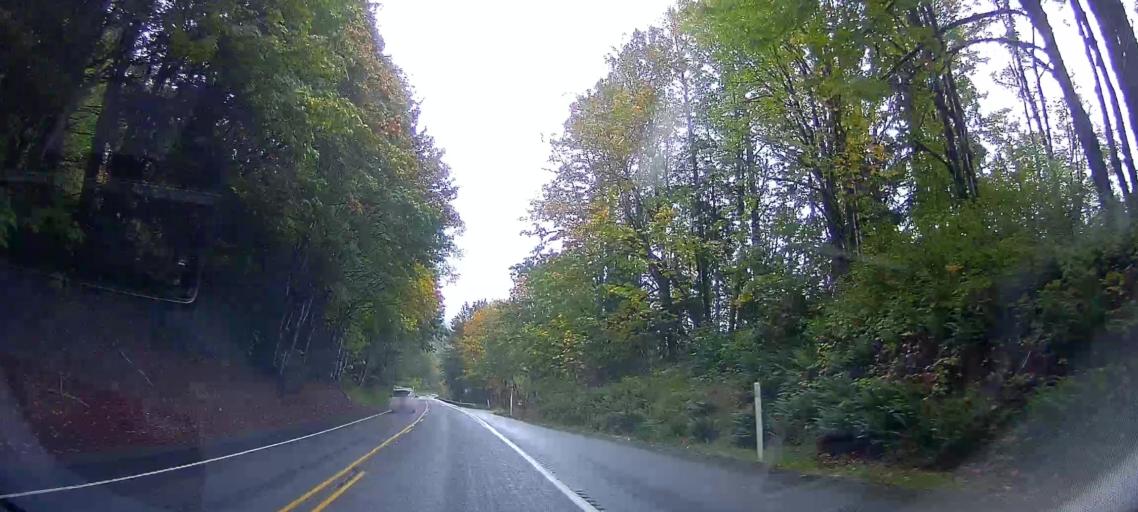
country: US
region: Washington
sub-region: Snohomish County
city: Darrington
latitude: 48.5406
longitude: -121.8040
